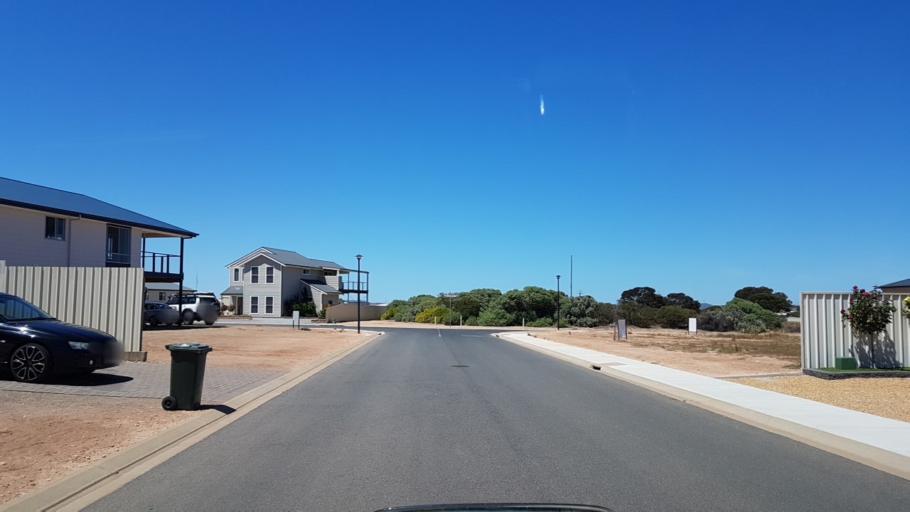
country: AU
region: South Australia
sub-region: Copper Coast
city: Wallaroo
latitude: -33.8943
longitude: 137.6301
